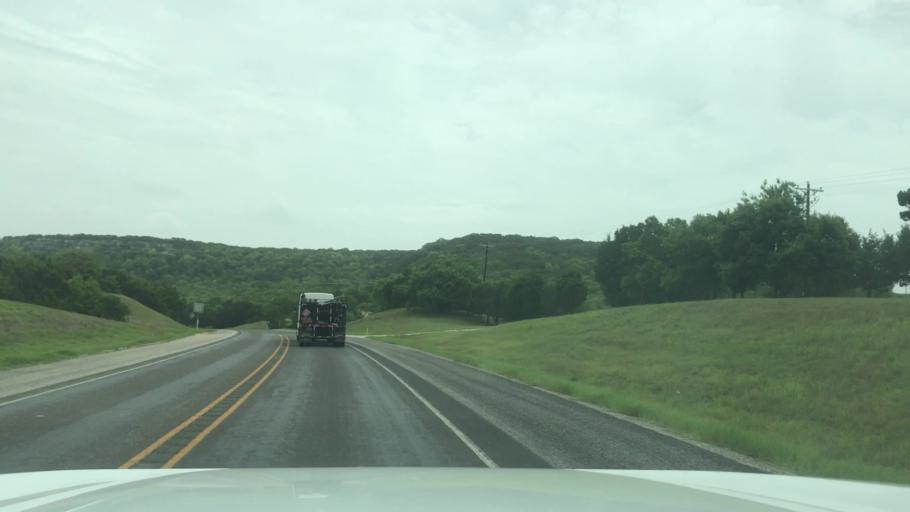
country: US
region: Texas
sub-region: Bosque County
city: Meridian
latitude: 31.9039
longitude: -97.6604
